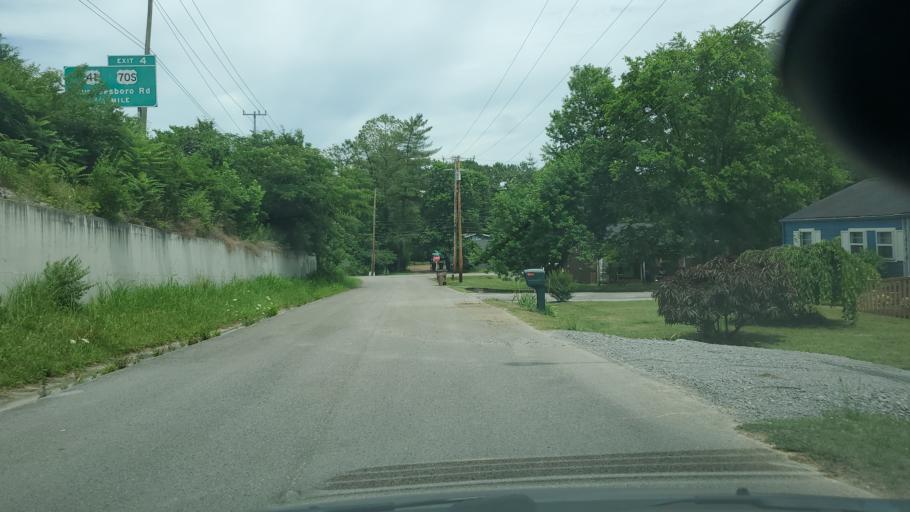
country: US
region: Tennessee
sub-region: Davidson County
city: Oak Hill
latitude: 36.1106
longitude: -86.7134
